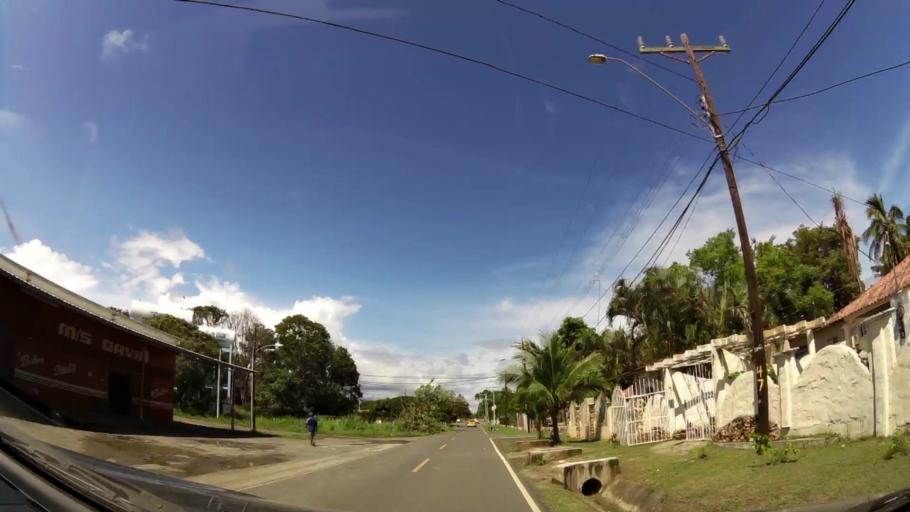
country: PA
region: Panama
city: Nueva Gorgona
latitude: 8.5561
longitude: -79.8751
